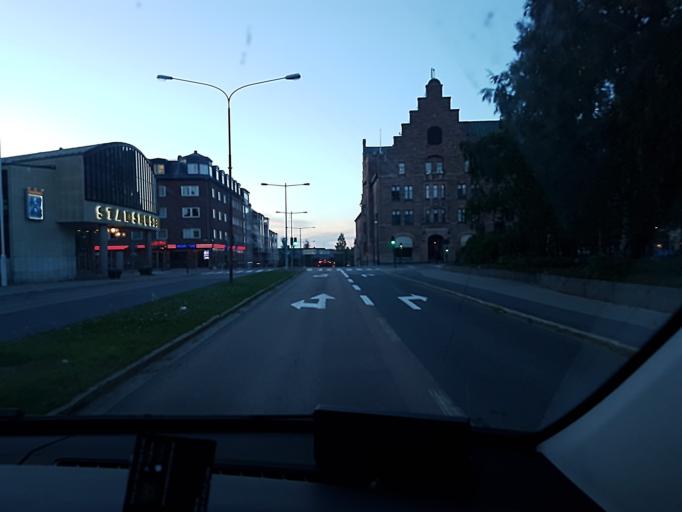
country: SE
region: Norrbotten
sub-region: Lulea Kommun
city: Lulea
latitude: 65.5829
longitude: 22.1449
